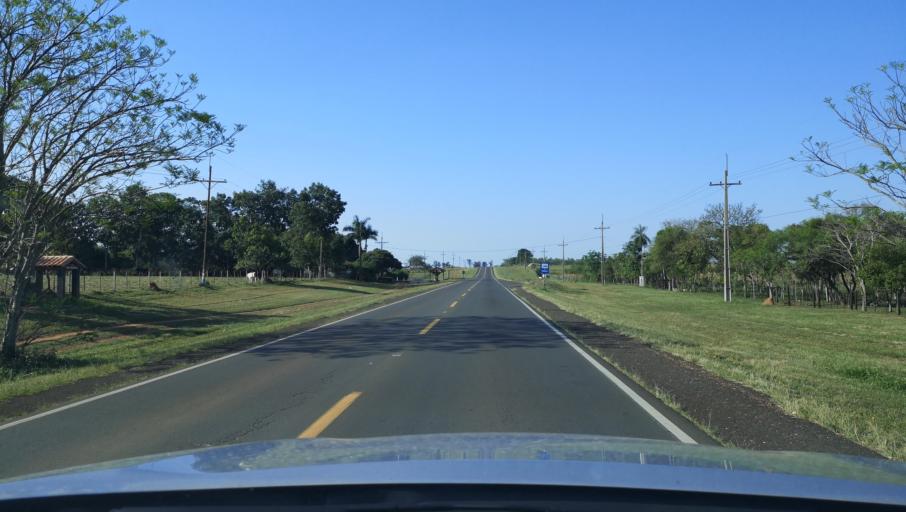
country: PY
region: Misiones
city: Santa Maria
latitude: -26.8166
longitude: -57.0244
